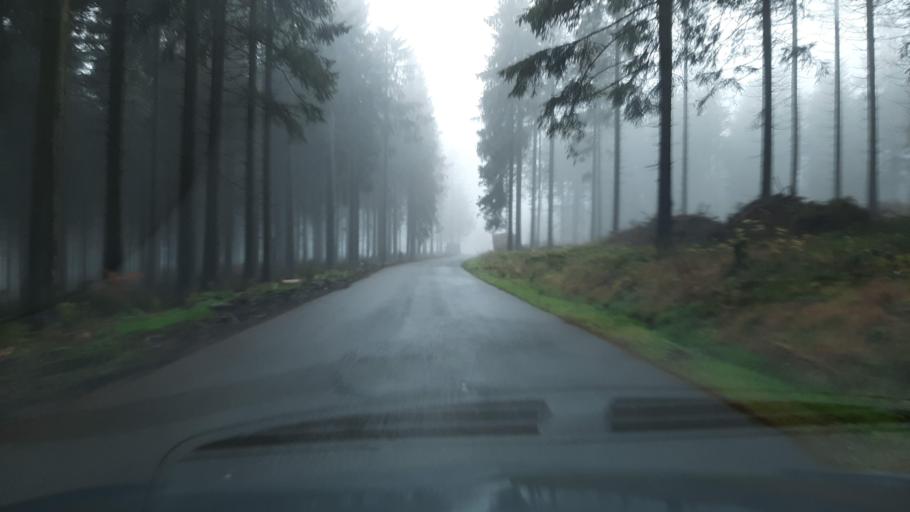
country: DE
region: North Rhine-Westphalia
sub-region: Regierungsbezirk Arnsberg
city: Winterberg
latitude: 51.1744
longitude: 8.4919
